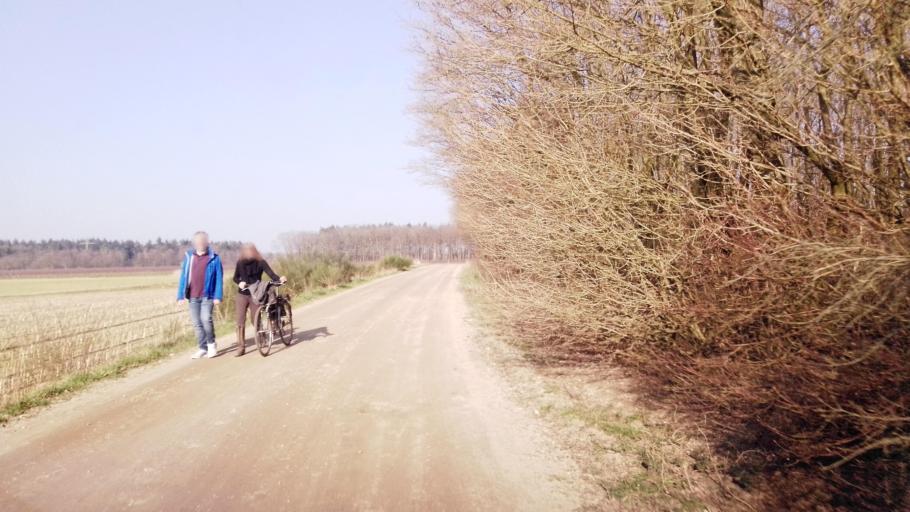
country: NL
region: Limburg
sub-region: Gemeente Beesel
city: Reuver
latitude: 51.3123
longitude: 6.0815
